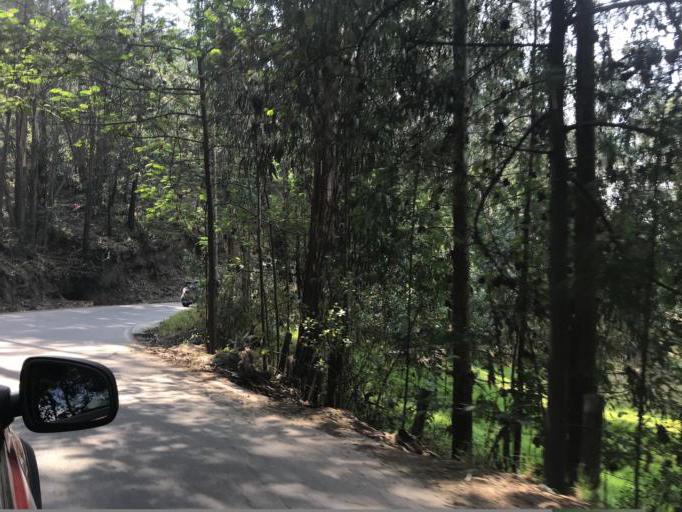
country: CO
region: Boyaca
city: Samaca
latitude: 5.4852
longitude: -73.4777
